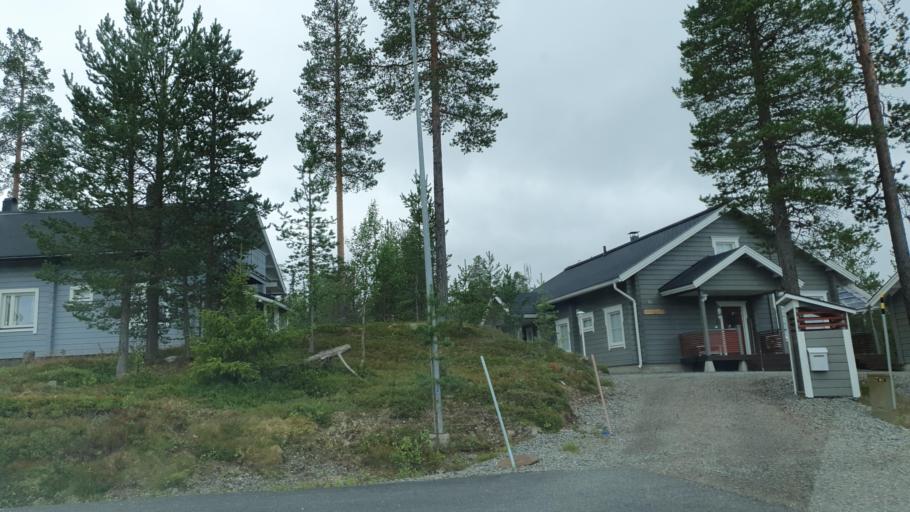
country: FI
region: Lapland
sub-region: Tunturi-Lappi
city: Kolari
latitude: 67.5935
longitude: 24.1700
